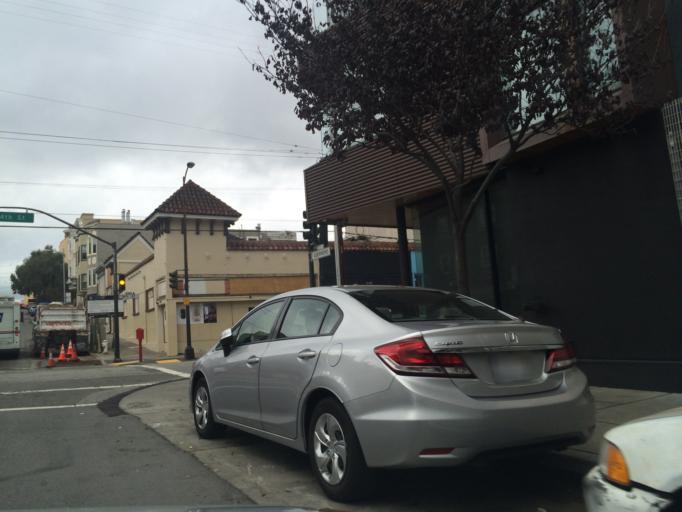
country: US
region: California
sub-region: San Francisco County
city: San Francisco
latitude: 37.7678
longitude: -122.4244
